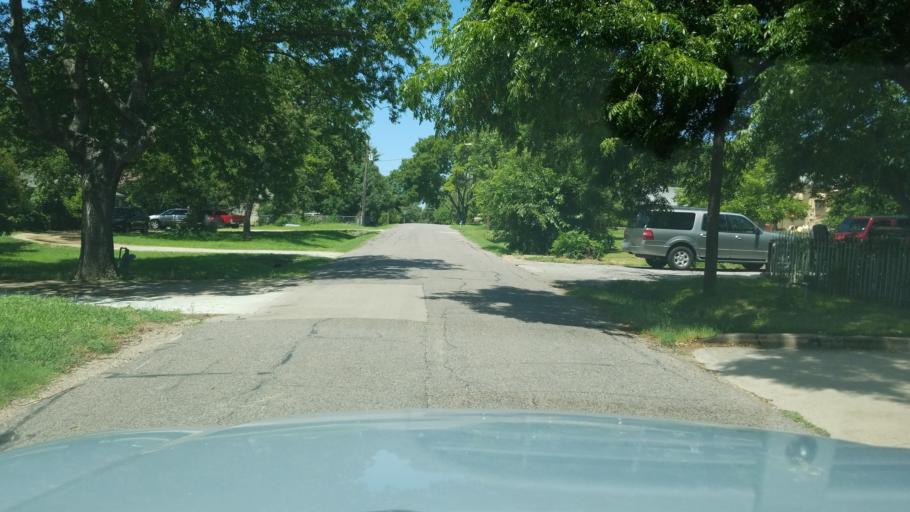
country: US
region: Texas
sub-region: Dallas County
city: Irving
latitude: 32.8036
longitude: -96.9276
